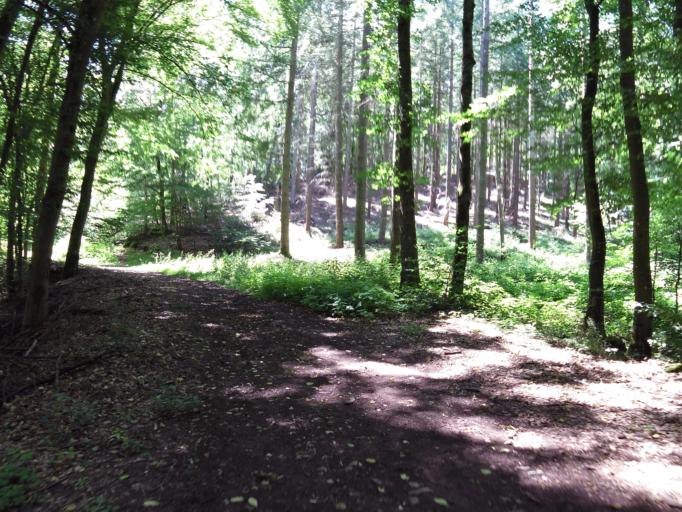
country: DE
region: Rheinland-Pfalz
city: Altleiningen
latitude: 49.4838
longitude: 8.0751
